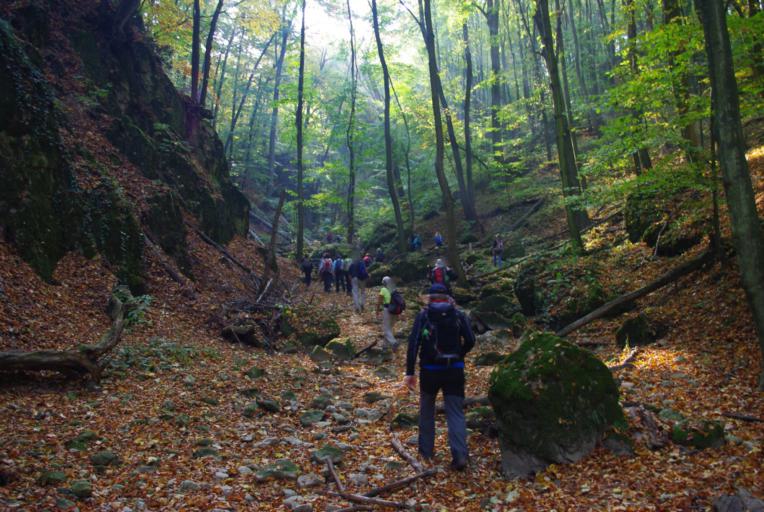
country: HU
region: Veszprem
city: Zirc
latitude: 47.3284
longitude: 17.9103
